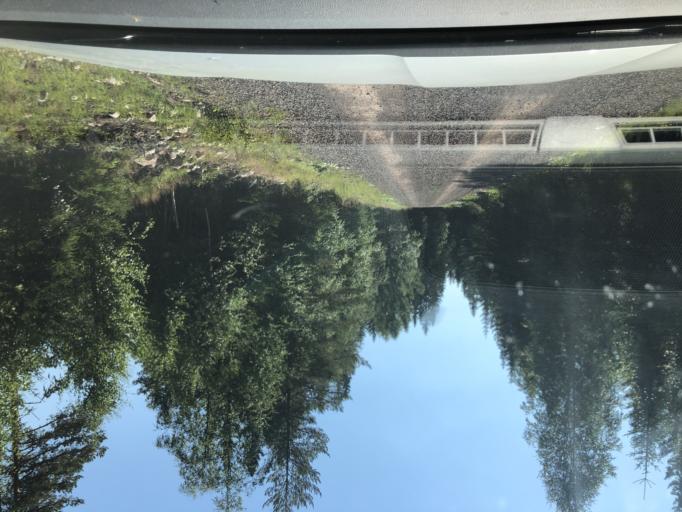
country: SE
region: Dalarna
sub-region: Orsa Kommun
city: Orsa
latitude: 61.2608
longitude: 14.7326
